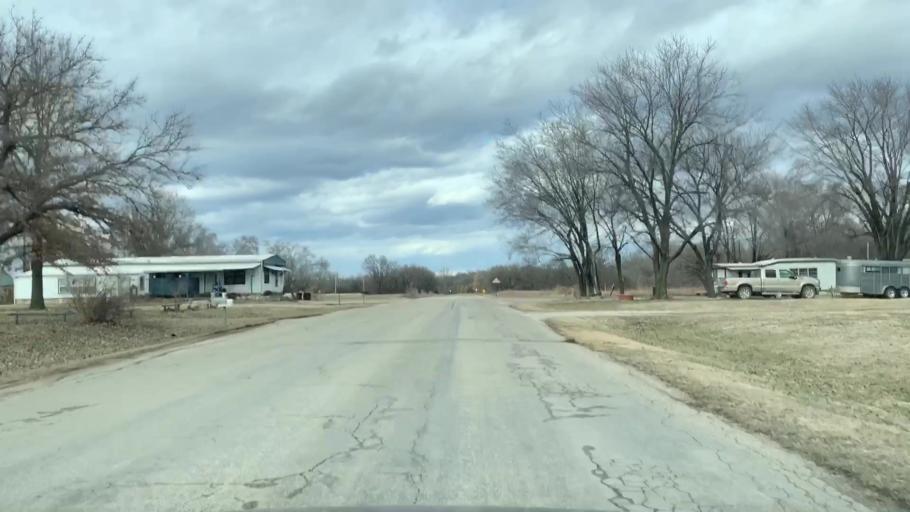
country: US
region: Kansas
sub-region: Neosho County
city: Chanute
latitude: 37.7450
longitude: -95.4704
